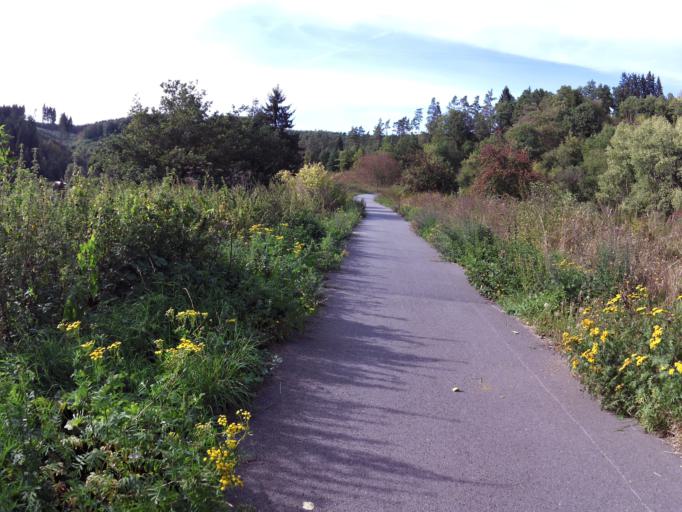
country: BE
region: Wallonia
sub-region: Province de Liege
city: Saint-Vith
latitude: 50.2346
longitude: 6.1572
